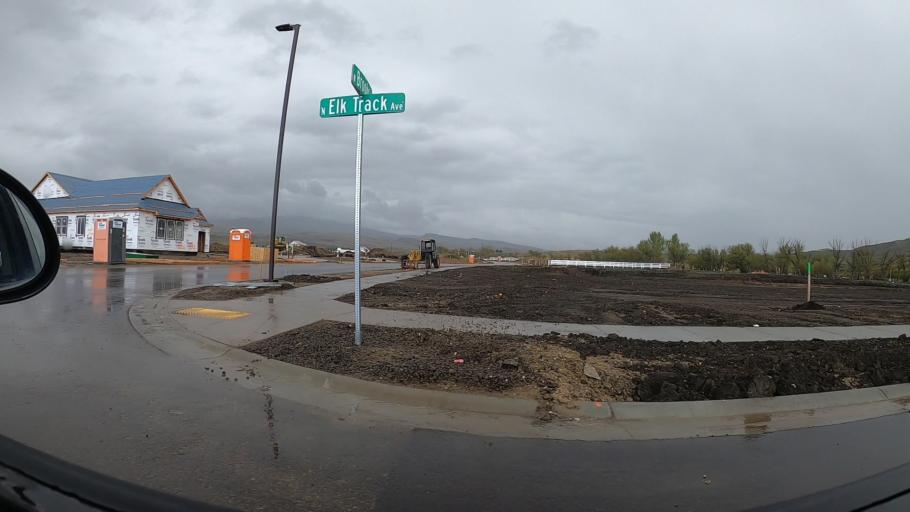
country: US
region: Idaho
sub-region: Ada County
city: Eagle
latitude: 43.7331
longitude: -116.2862
